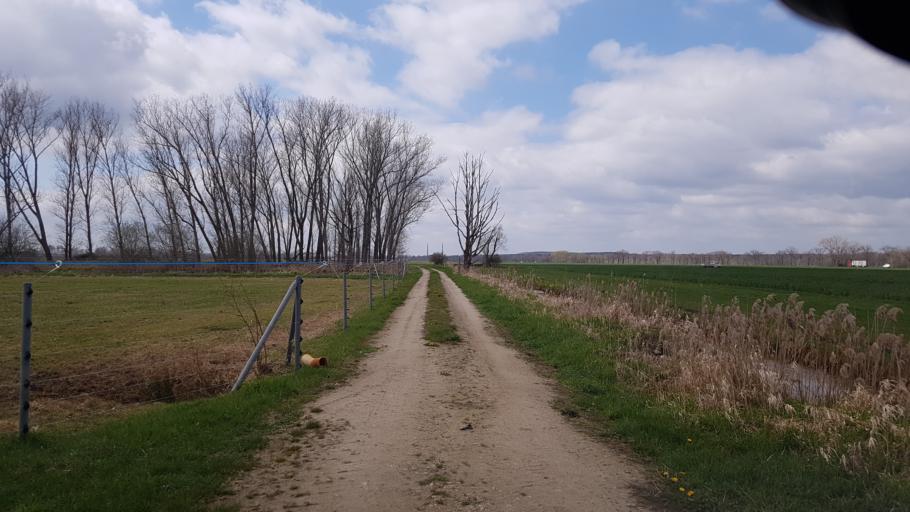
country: DE
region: Brandenburg
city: Schraden
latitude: 51.4666
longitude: 13.6836
